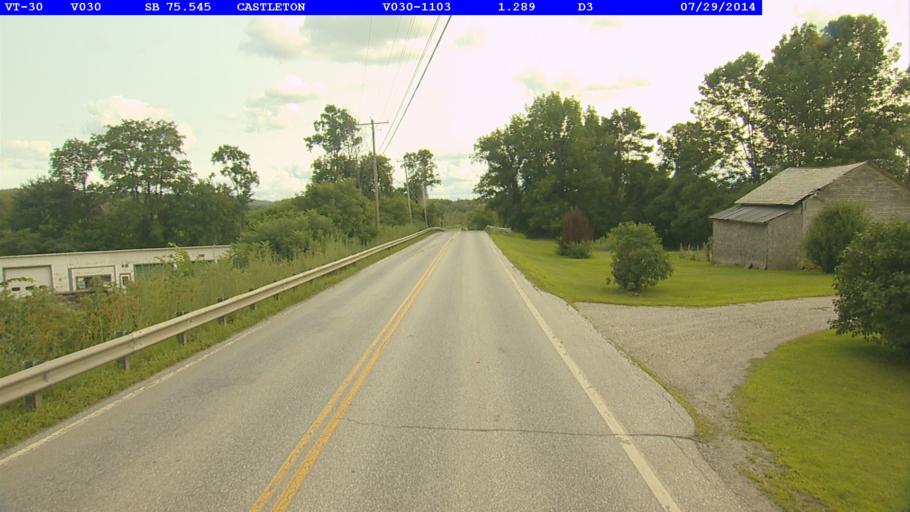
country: US
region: Vermont
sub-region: Rutland County
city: Castleton
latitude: 43.6053
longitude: -73.2092
